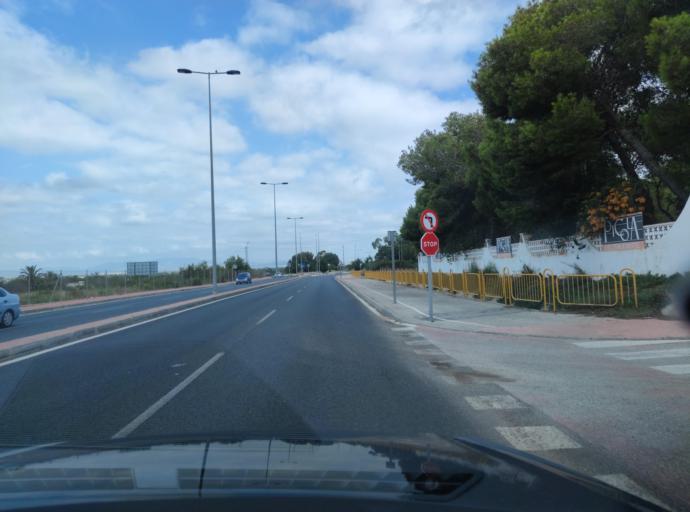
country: ES
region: Valencia
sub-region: Provincia de Alicante
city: Santa Pola
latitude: 38.2084
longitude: -0.5852
